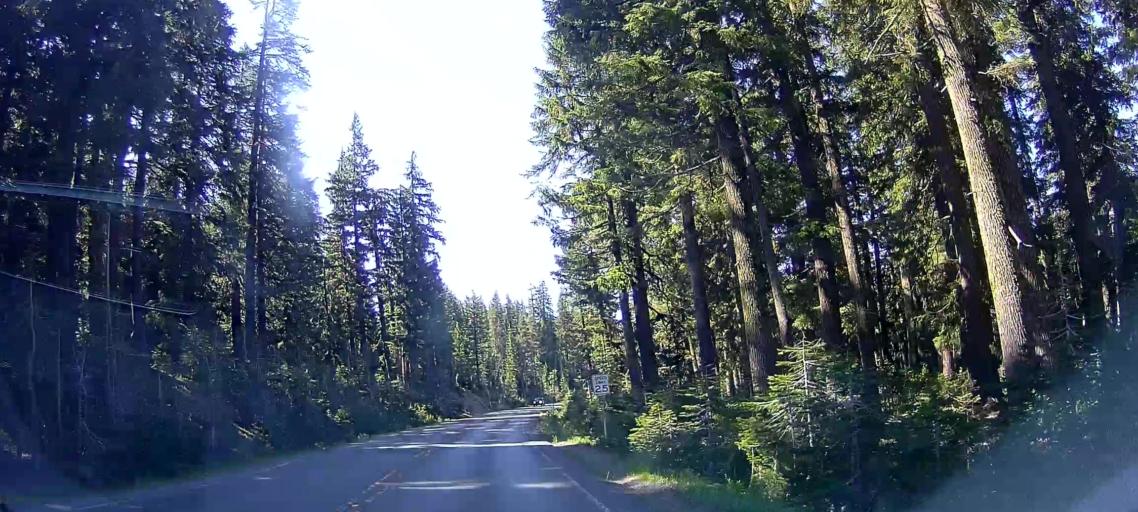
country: US
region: Oregon
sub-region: Jackson County
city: Shady Cove
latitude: 42.8993
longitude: -122.1330
